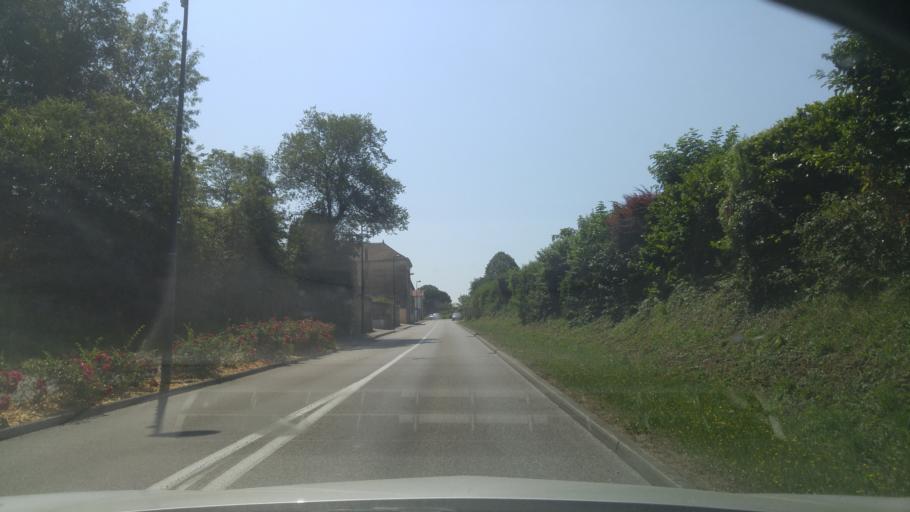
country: FR
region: Rhone-Alpes
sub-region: Departement de l'Isere
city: Tignieu-Jameyzieu
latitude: 45.7402
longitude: 5.1792
